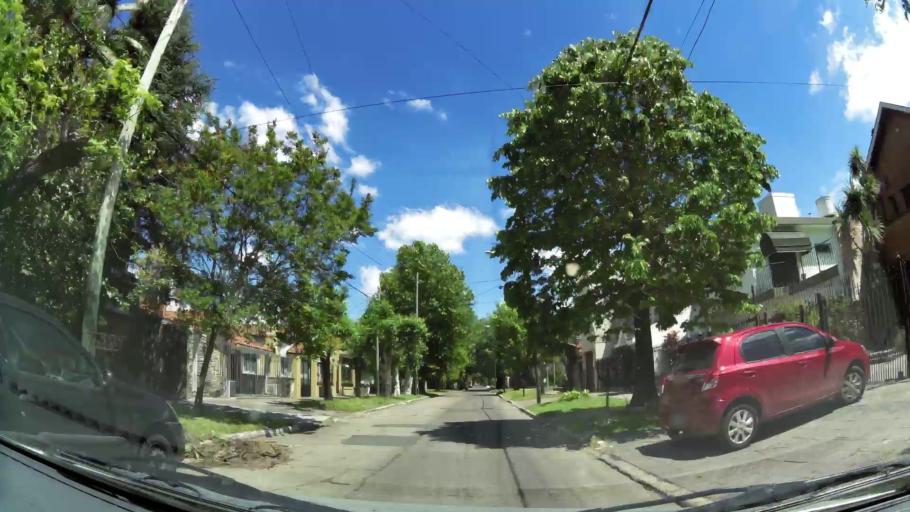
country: AR
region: Buenos Aires
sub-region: Partido de Lomas de Zamora
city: Lomas de Zamora
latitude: -34.7423
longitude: -58.4063
